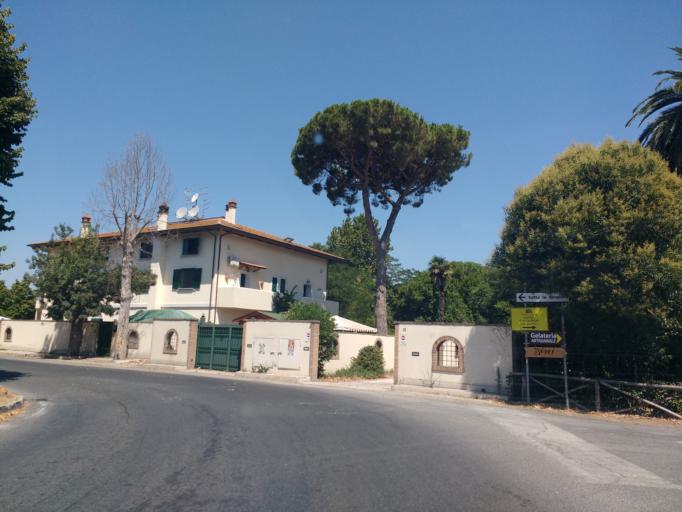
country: IT
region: Latium
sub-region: Citta metropolitana di Roma Capitale
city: Maccarese
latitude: 41.8776
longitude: 12.2146
